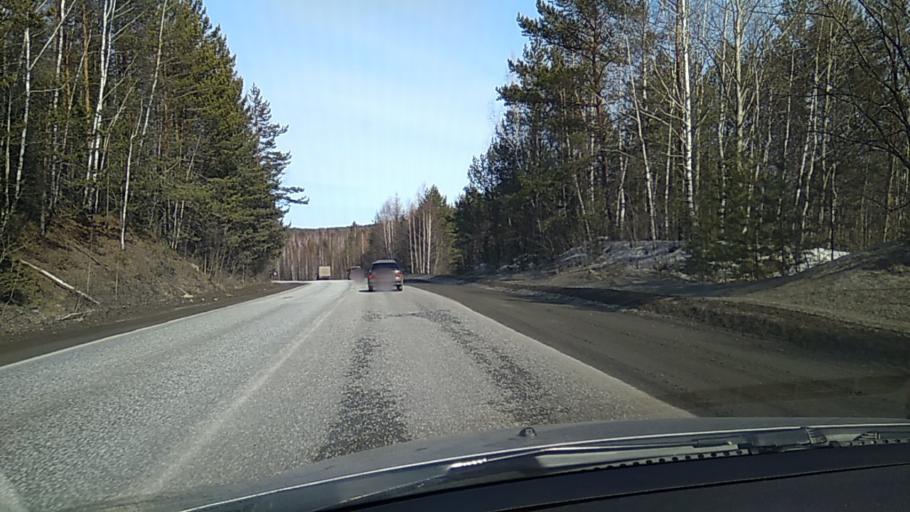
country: RU
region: Sverdlovsk
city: Chernoistochinsk
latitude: 57.7798
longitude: 59.8950
